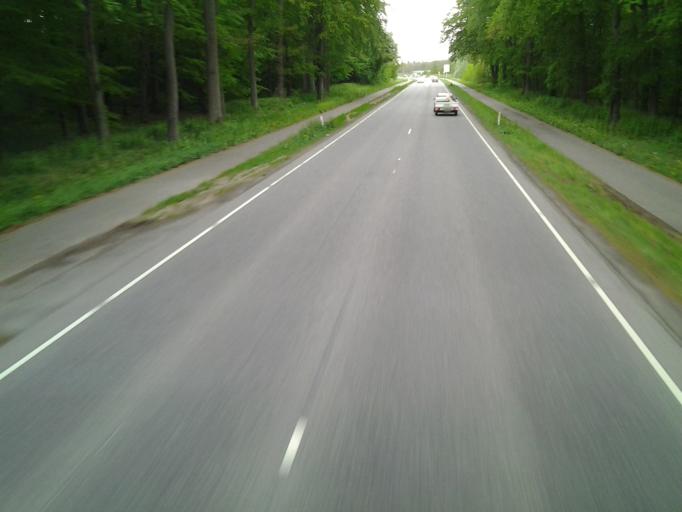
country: DK
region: Zealand
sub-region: Guldborgsund Kommune
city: Nykobing Falster
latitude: 54.7416
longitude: 11.9180
